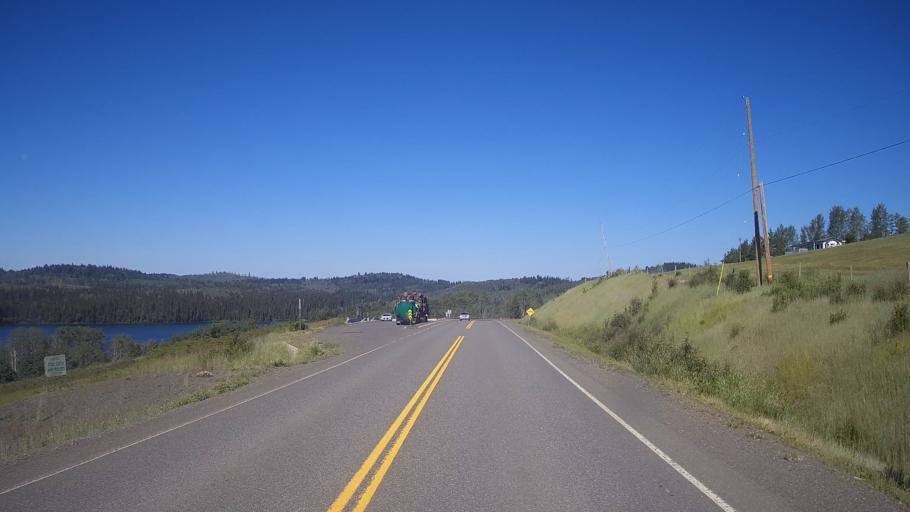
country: CA
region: British Columbia
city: Kamloops
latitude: 51.4984
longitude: -120.5920
